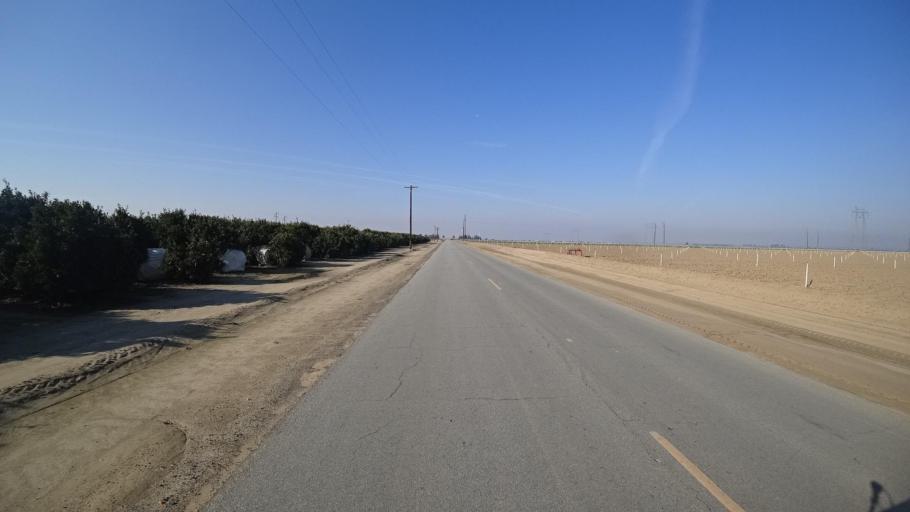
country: US
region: California
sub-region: Kern County
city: Weedpatch
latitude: 35.1220
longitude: -118.9741
